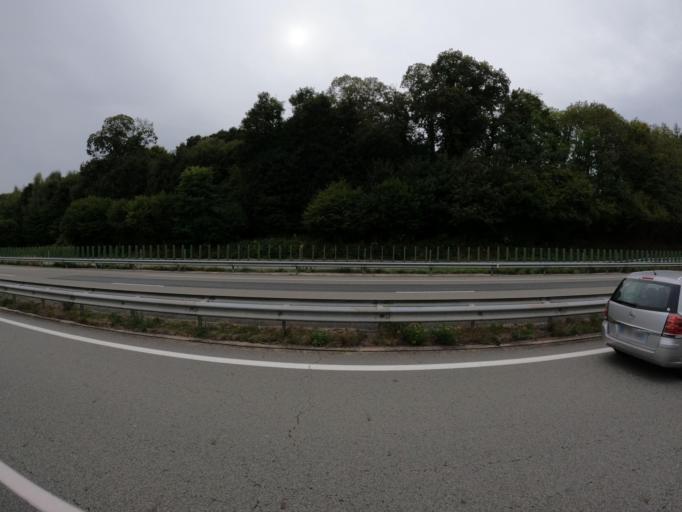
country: FR
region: Limousin
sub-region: Departement de la Creuse
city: Saint-Vaury
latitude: 46.2106
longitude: 1.7471
